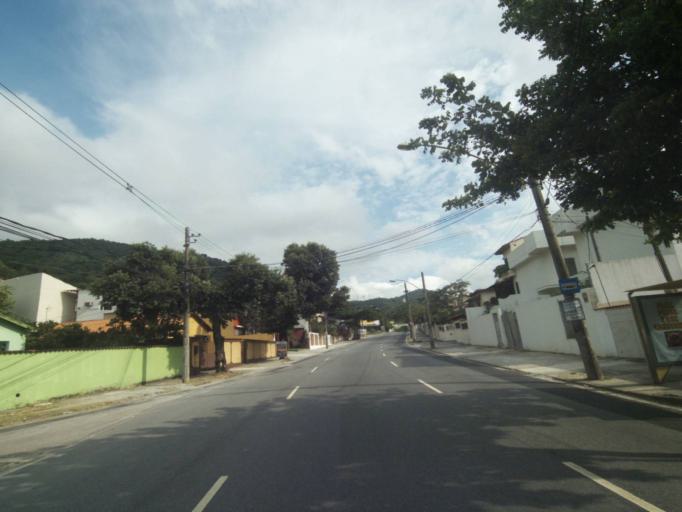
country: BR
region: Rio de Janeiro
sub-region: Nilopolis
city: Nilopolis
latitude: -22.8915
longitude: -43.3944
